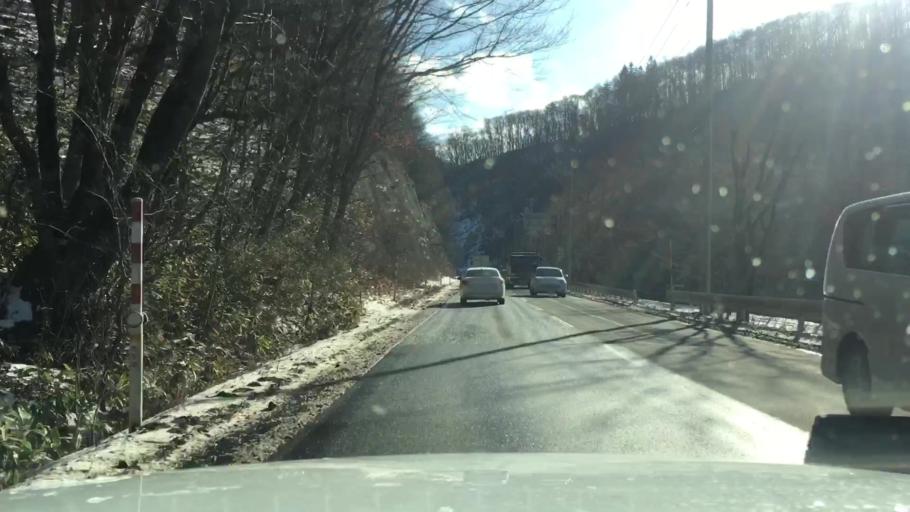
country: JP
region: Iwate
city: Morioka-shi
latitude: 39.6324
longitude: 141.4547
